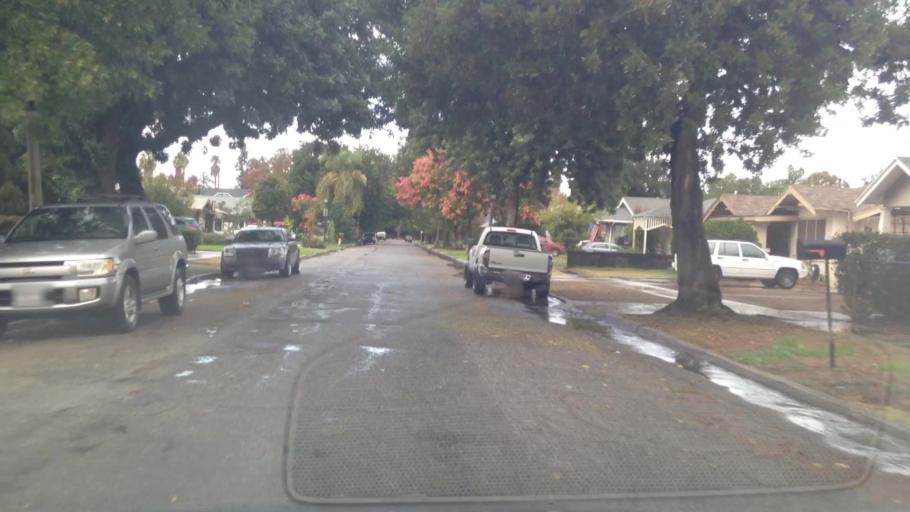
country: US
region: California
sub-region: Riverside County
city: Riverside
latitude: 33.9412
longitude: -117.4044
